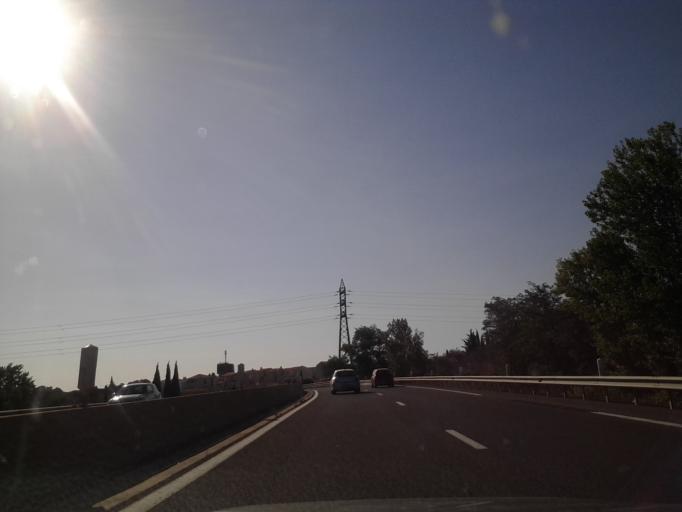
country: FR
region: Languedoc-Roussillon
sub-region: Departement des Pyrenees-Orientales
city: Pezilla-la-Riviere
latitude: 42.6821
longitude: 2.7747
